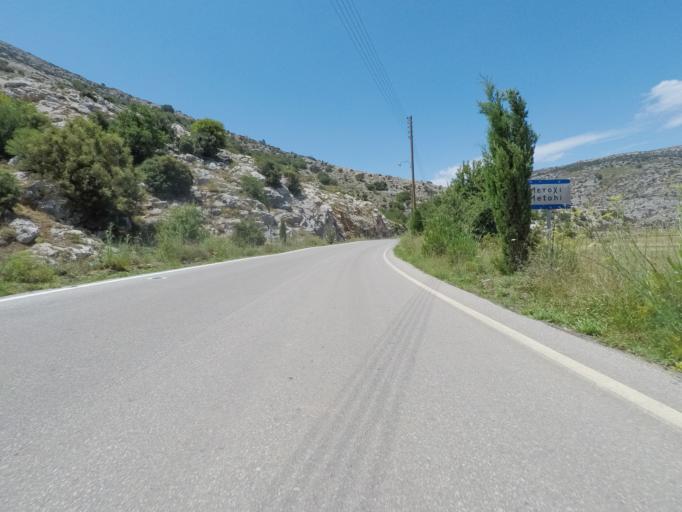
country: GR
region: Crete
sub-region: Nomos Irakleiou
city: Mokhos
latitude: 35.1865
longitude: 25.4316
